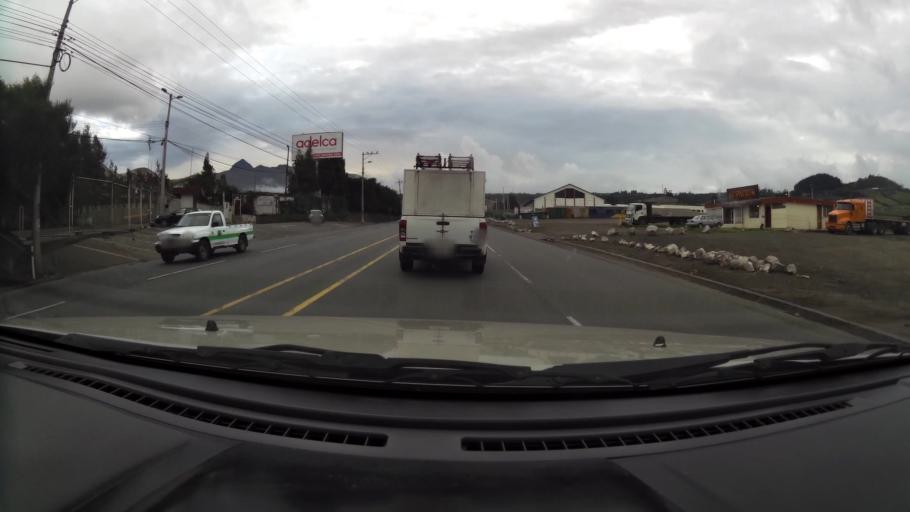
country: EC
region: Pichincha
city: Machachi
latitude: -0.4486
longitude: -78.6567
